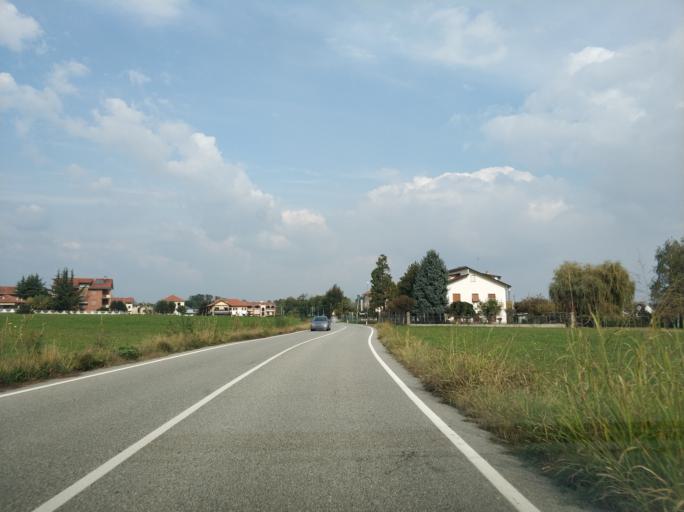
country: IT
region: Piedmont
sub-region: Provincia di Torino
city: San Carlo Canavese
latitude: 45.2447
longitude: 7.6145
